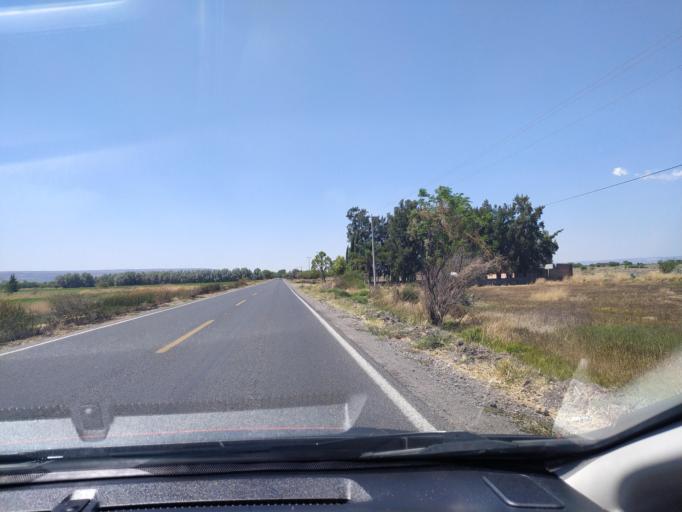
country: MX
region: Guanajuato
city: Ciudad Manuel Doblado
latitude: 20.7434
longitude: -101.8919
